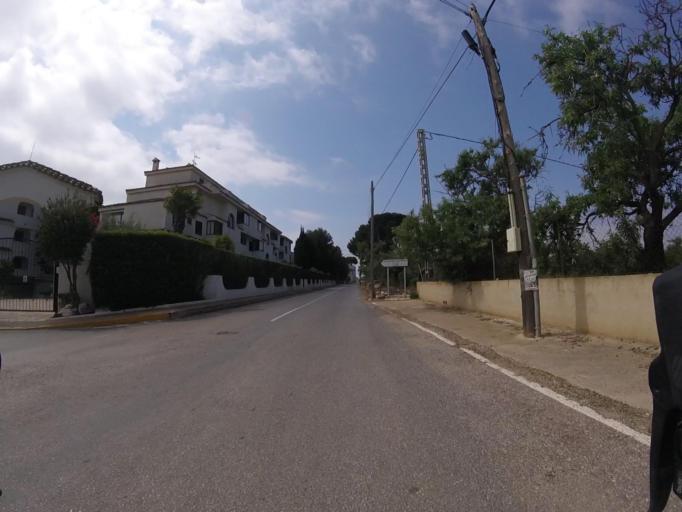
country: ES
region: Valencia
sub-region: Provincia de Castello
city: Alcoceber
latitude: 40.2399
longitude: 0.2684
